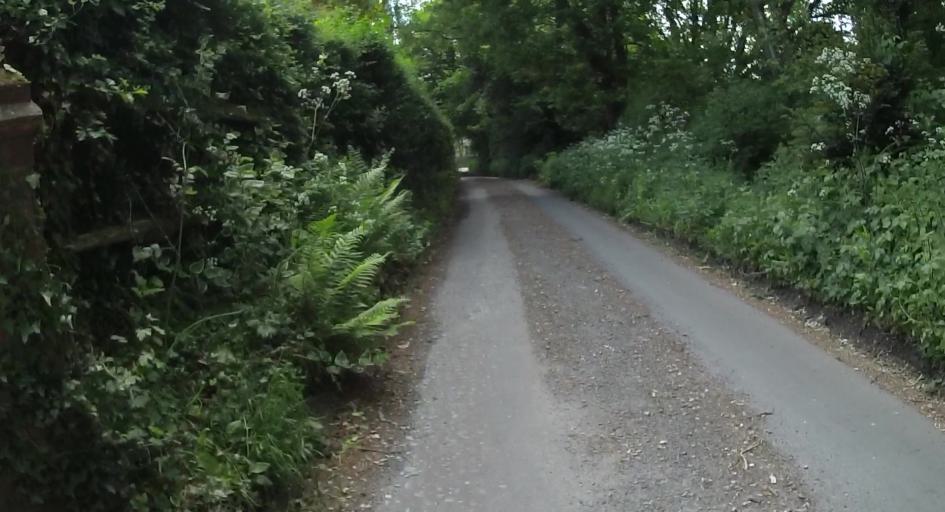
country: GB
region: England
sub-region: Surrey
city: Farnham
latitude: 51.2350
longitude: -0.8434
